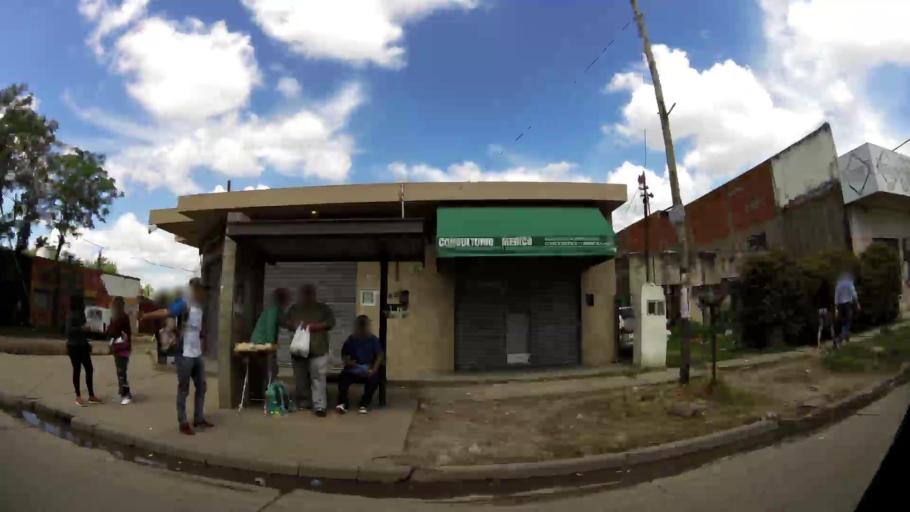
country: AR
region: Buenos Aires
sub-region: Partido de Quilmes
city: Quilmes
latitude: -34.8057
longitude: -58.2488
